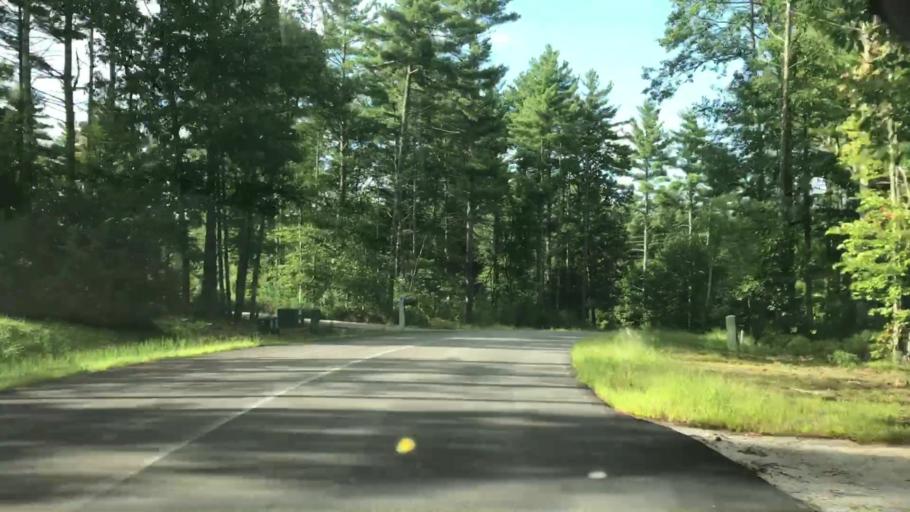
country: US
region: New Hampshire
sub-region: Hillsborough County
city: Milford
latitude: 42.8519
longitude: -71.5825
